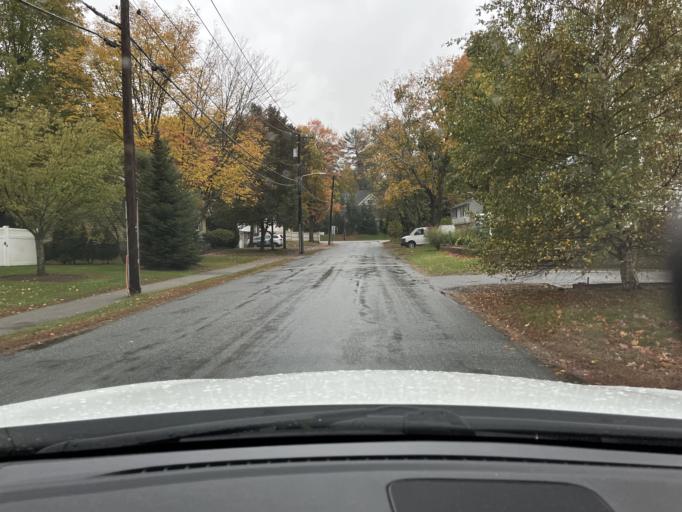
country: US
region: Massachusetts
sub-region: Norfolk County
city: Wellesley
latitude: 42.2991
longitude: -71.2831
